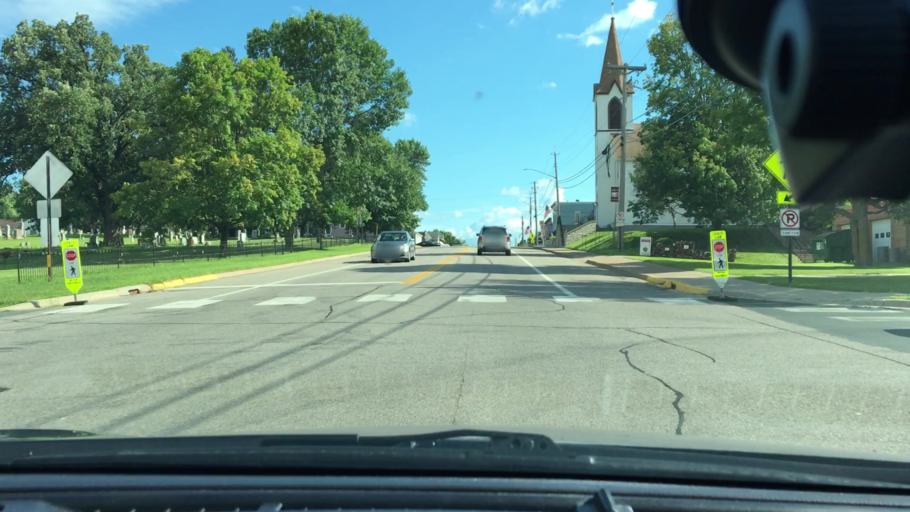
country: US
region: Minnesota
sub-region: Hennepin County
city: Saint Bonifacius
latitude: 44.9056
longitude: -93.7473
